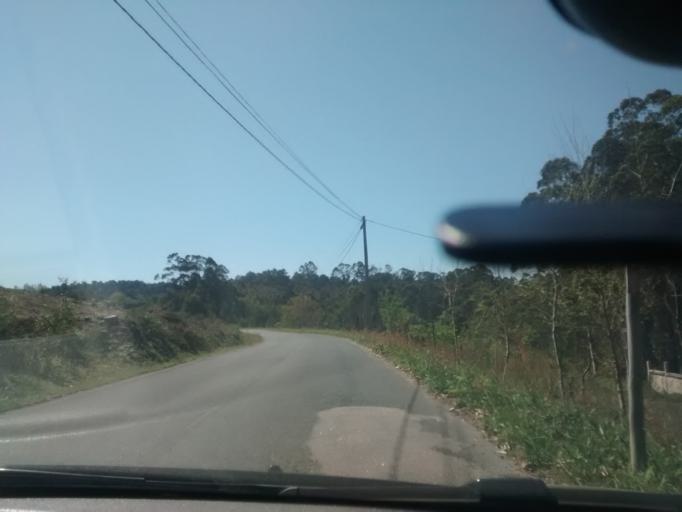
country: ES
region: Galicia
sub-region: Provincia de Pontevedra
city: O Grove
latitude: 42.4794
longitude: -8.8804
